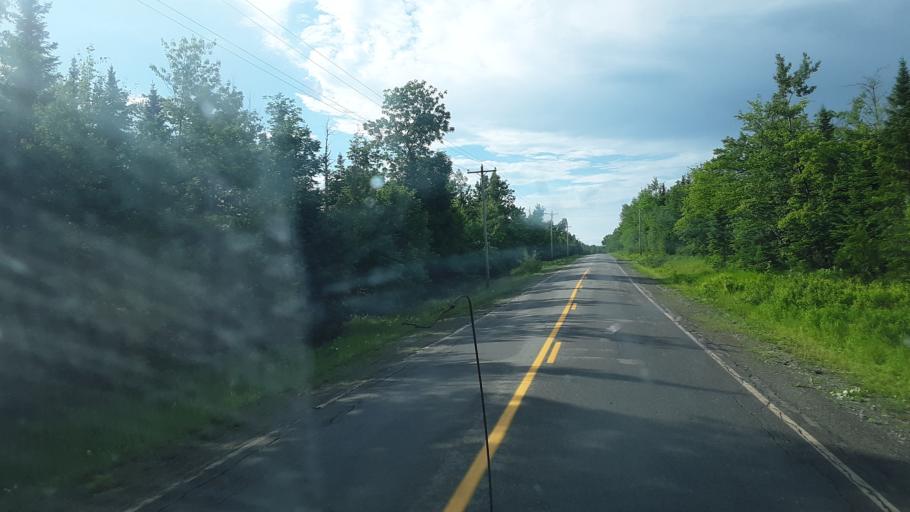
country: US
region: Maine
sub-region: Washington County
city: Calais
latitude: 45.1979
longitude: -67.5255
